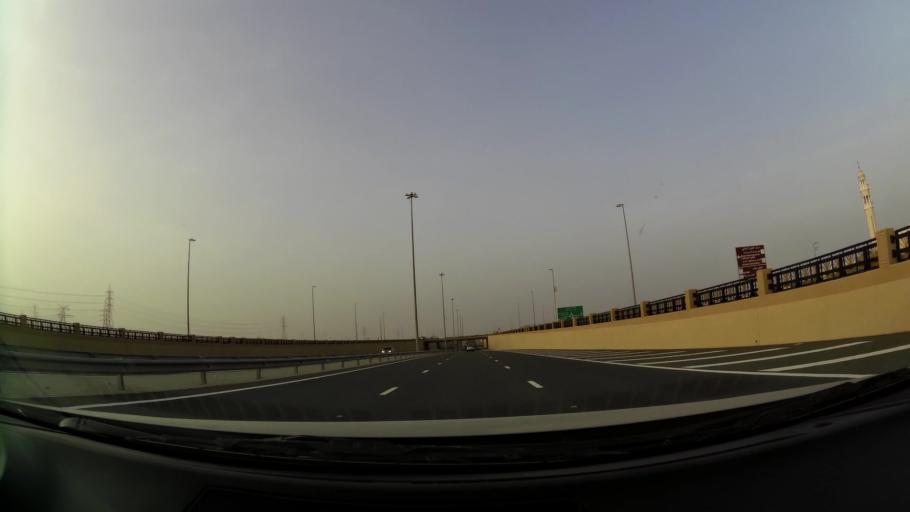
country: OM
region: Al Buraimi
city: Al Buraymi
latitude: 24.3170
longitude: 55.7512
